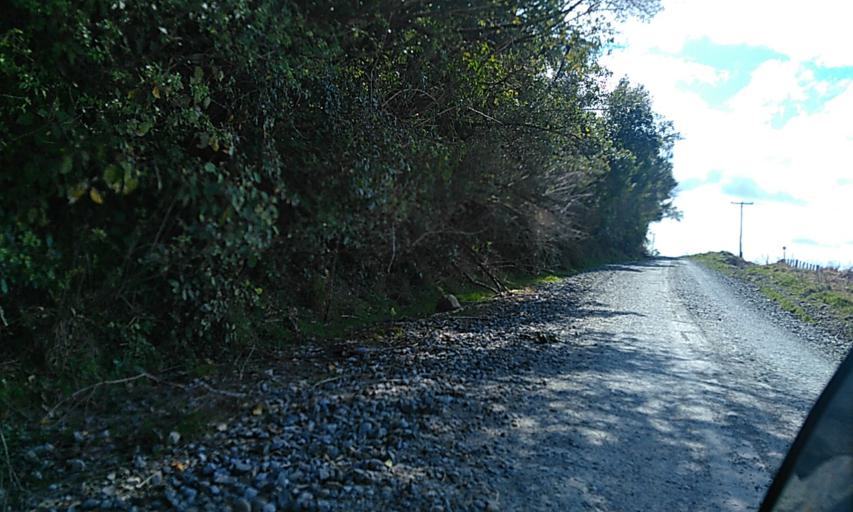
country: NZ
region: Gisborne
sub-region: Gisborne District
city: Gisborne
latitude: -38.2286
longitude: 178.0680
